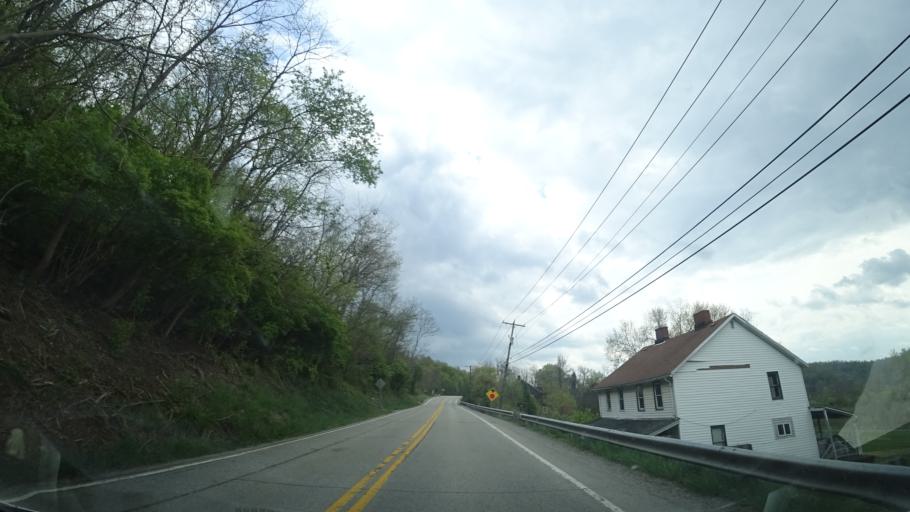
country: US
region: Pennsylvania
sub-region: Fayette County
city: Fairhope
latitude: 40.1087
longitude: -79.8426
